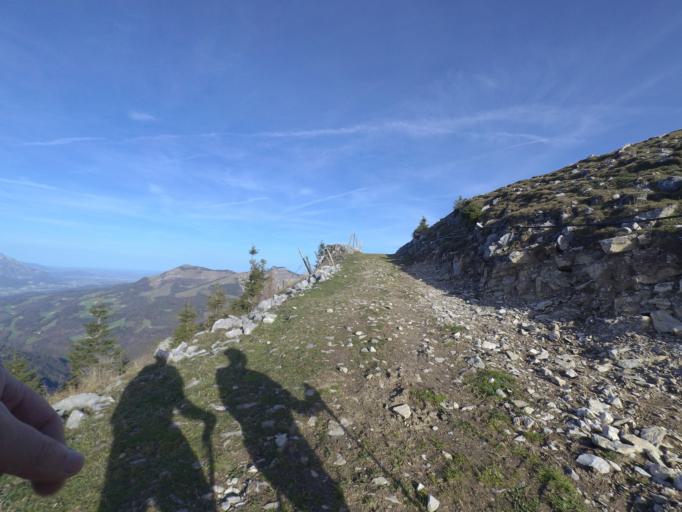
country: AT
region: Salzburg
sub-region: Politischer Bezirk Salzburg-Umgebung
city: Hintersee
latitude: 47.6392
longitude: 13.2682
